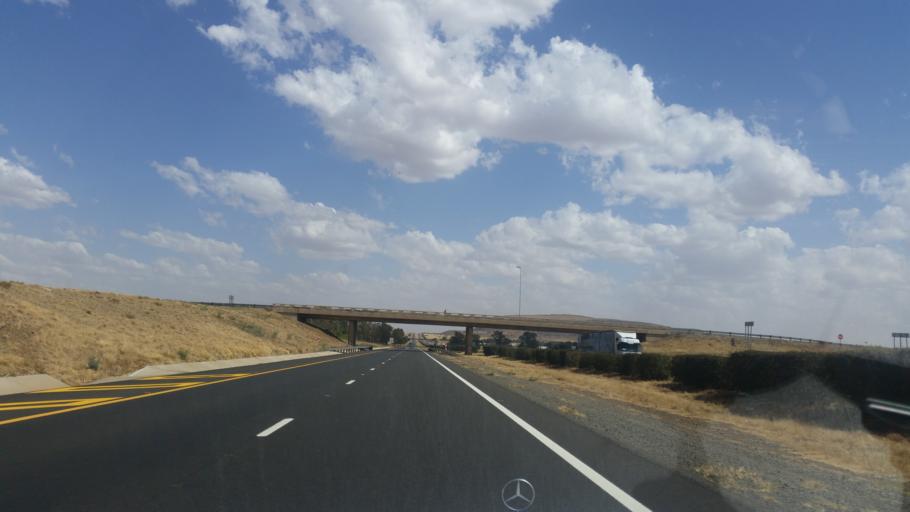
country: ZA
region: Orange Free State
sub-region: Mangaung Metropolitan Municipality
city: Bloemfontein
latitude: -29.1999
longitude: 26.1914
